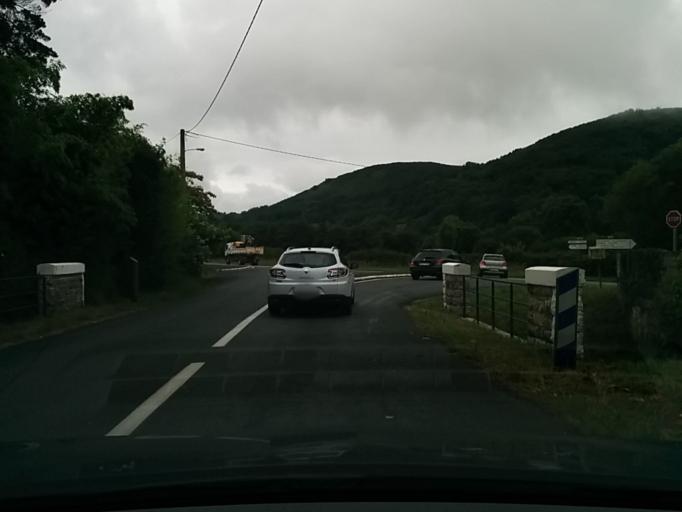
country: FR
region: Aquitaine
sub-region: Departement des Pyrenees-Atlantiques
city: Saint-Pee-sur-Nivelle
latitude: 43.3617
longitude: -1.5836
